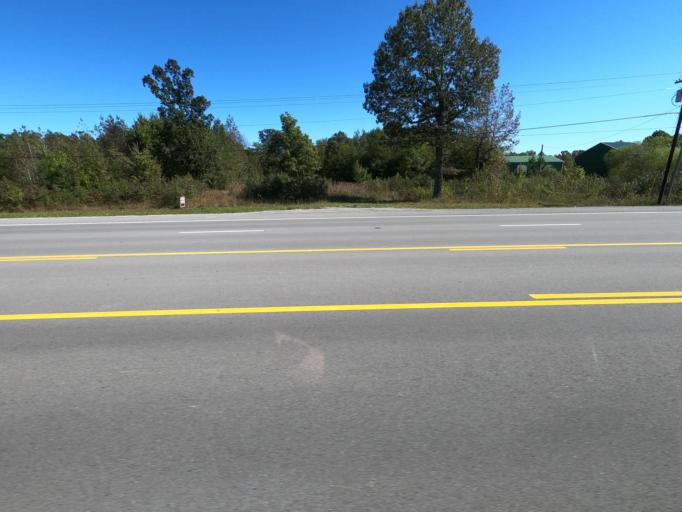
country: US
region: Tennessee
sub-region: Maury County
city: Mount Pleasant
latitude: 35.4342
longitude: -87.2806
